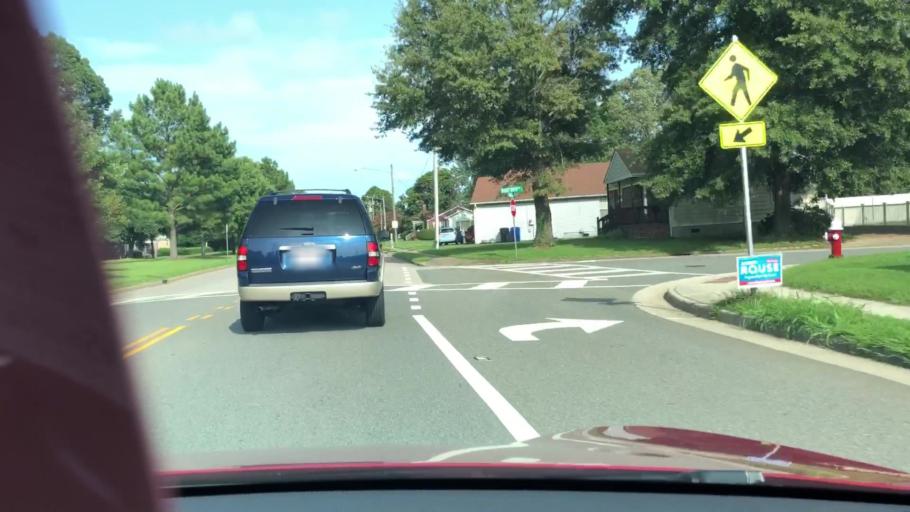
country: US
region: Virginia
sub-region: City of Virginia Beach
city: Virginia Beach
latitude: 36.8379
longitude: -75.9970
